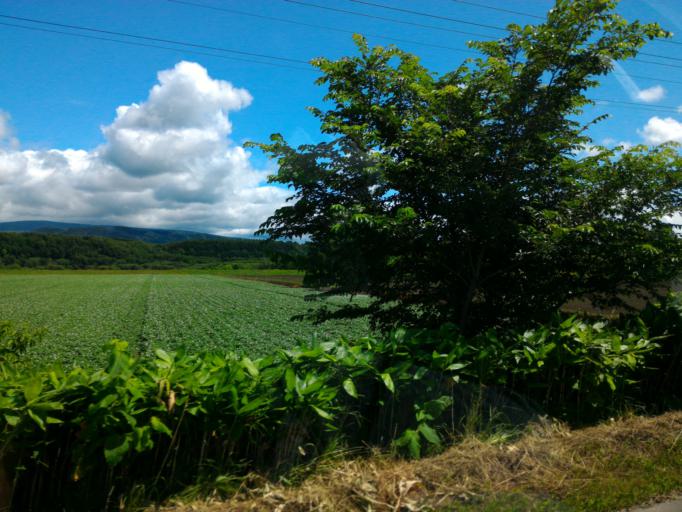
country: JP
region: Hokkaido
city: Nayoro
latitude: 44.5294
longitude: 142.3248
